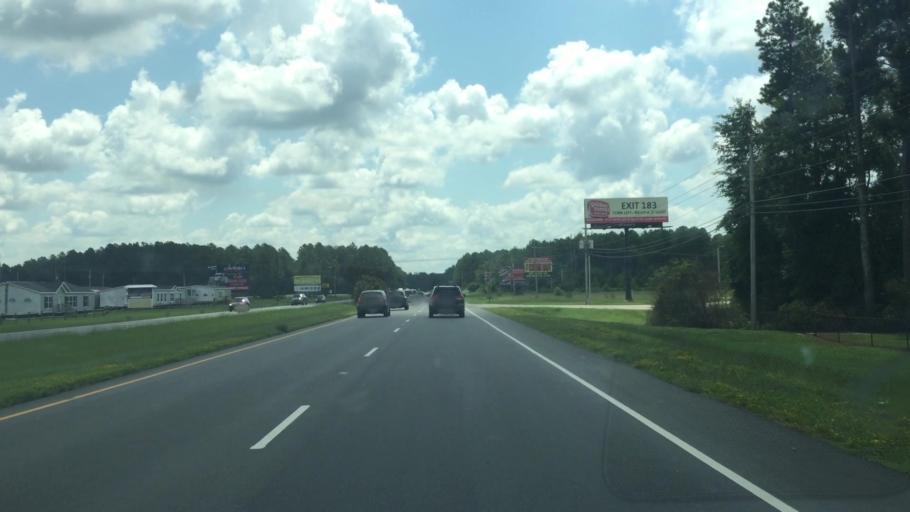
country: US
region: North Carolina
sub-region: Scotland County
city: Laurel Hill
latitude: 34.8048
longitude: -79.5414
